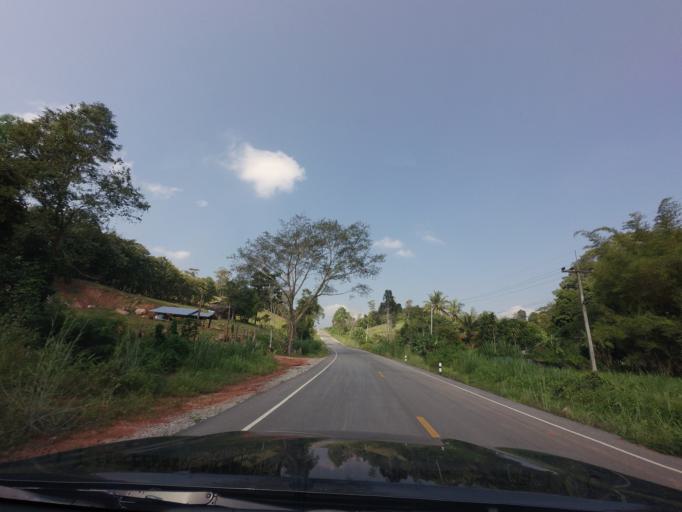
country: TH
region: Loei
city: Na Haeo
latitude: 17.4990
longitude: 101.0452
